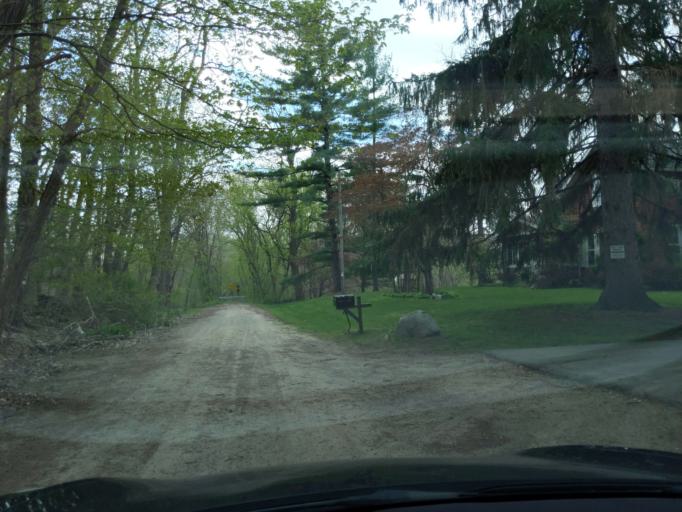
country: US
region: Michigan
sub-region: Eaton County
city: Dimondale
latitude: 42.6307
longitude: -84.6180
